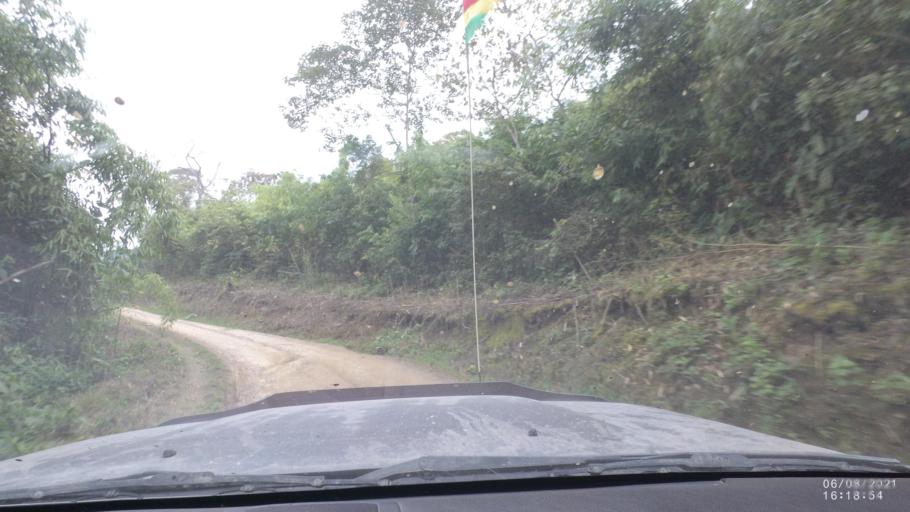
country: BO
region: La Paz
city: Quime
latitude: -16.5499
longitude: -66.7438
